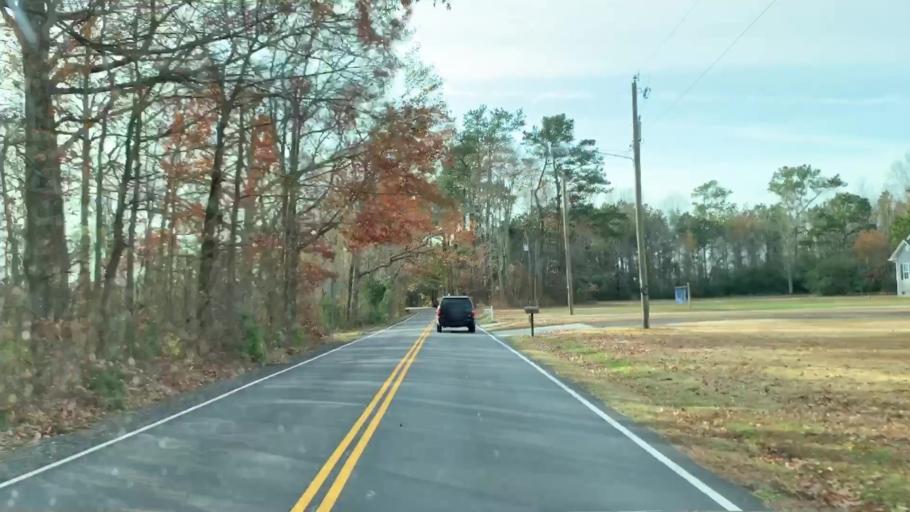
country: US
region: Virginia
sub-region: City of Virginia Beach
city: Virginia Beach
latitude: 36.6979
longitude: -76.0440
